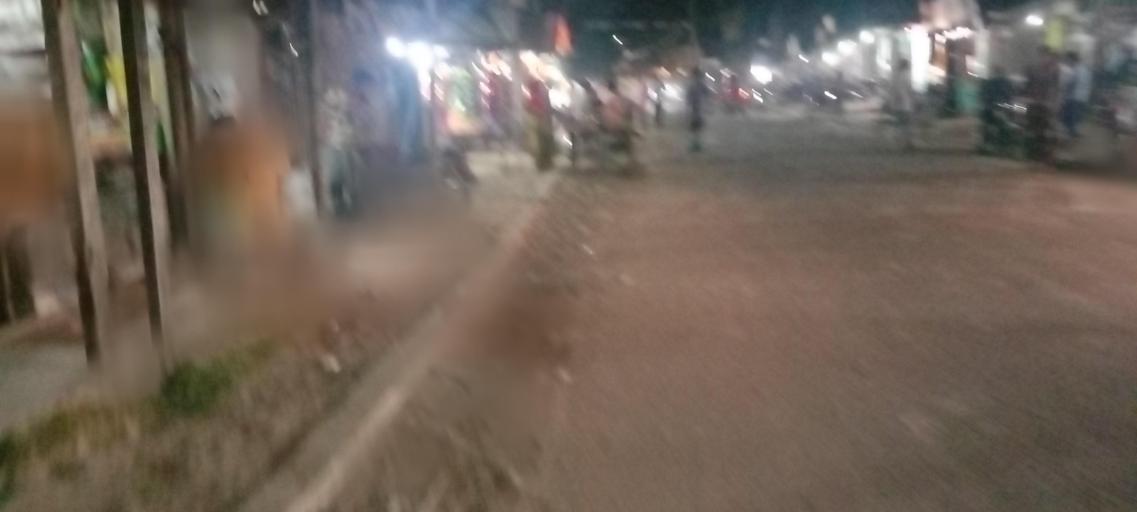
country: BD
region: Dhaka
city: Sakhipur
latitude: 24.4525
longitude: 90.2782
